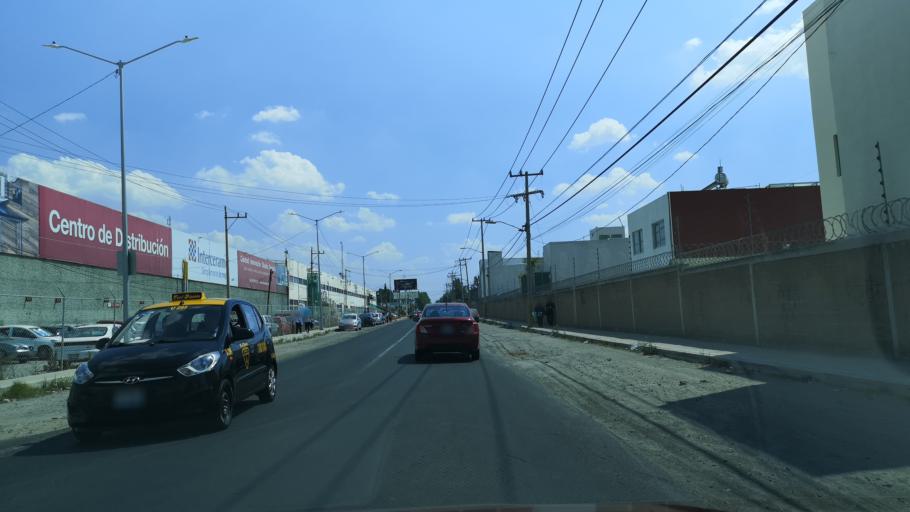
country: MX
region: Puebla
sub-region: Cuautlancingo
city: Sanctorum
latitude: 19.0830
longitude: -98.2156
